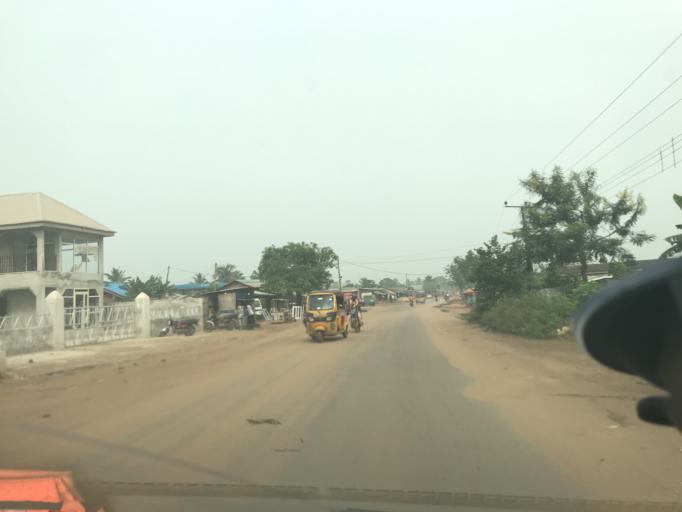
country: NG
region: Ogun
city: Ado Odo
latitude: 6.4977
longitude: 2.9556
